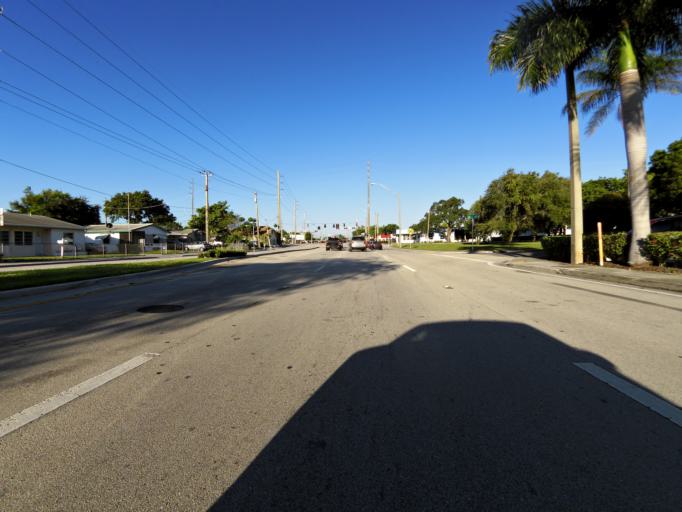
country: US
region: Florida
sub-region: Broward County
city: Dania Beach
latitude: 26.0488
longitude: -80.1456
